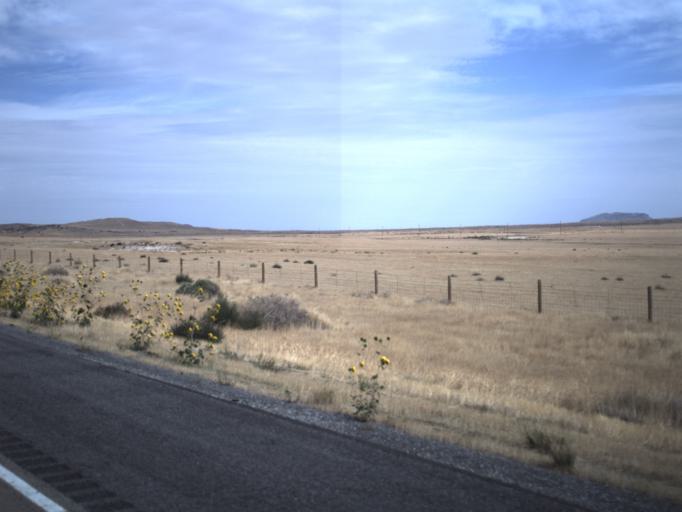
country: US
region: Utah
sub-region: Tooele County
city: Grantsville
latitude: 40.8078
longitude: -112.8632
